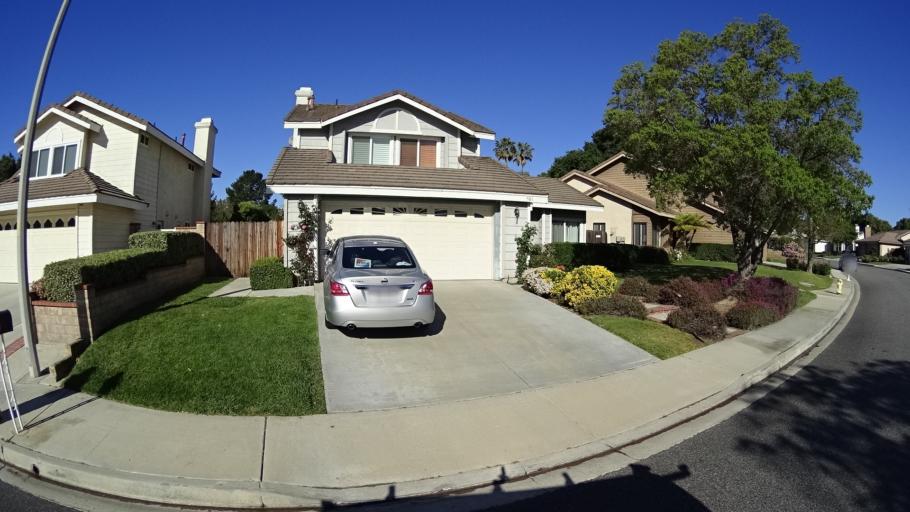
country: US
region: California
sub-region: Ventura County
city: Casa Conejo
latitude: 34.1877
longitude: -118.9085
